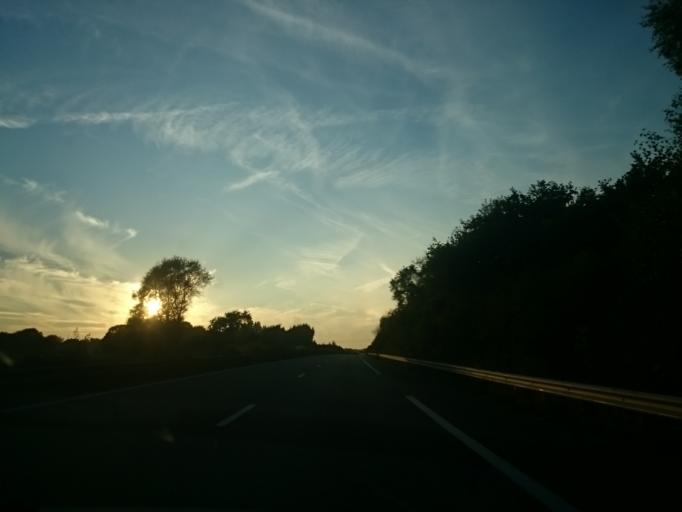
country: FR
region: Brittany
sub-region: Departement du Finistere
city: Quimperle
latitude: 47.8642
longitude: -3.5758
